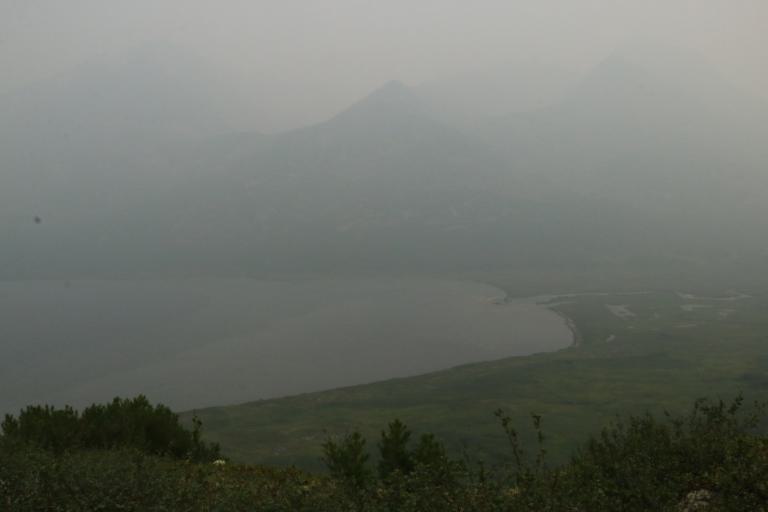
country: RU
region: Respublika Buryatiya
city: Kichera
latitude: 56.2450
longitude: 110.7736
